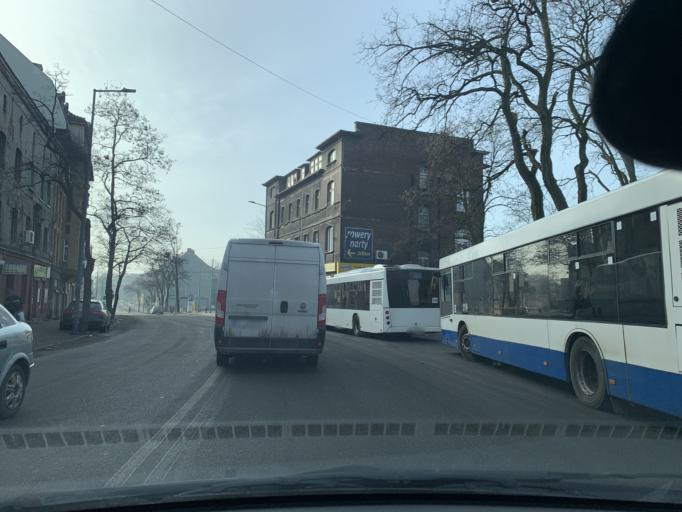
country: PL
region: Silesian Voivodeship
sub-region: Swietochlowice
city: Swietochlowice
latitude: 50.3385
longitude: 18.8690
